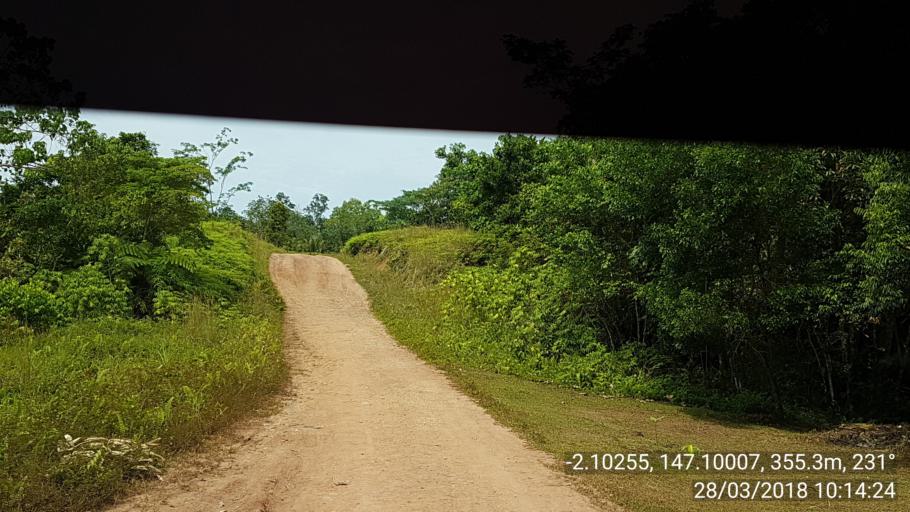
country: PG
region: Manus
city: Lorengau
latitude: -2.1025
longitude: 147.1000
